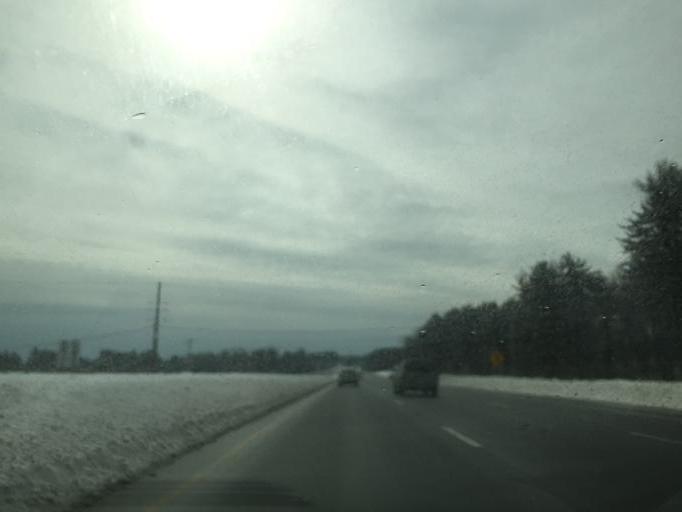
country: US
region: New Hampshire
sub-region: Strafford County
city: Rochester
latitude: 43.3114
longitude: -70.9962
